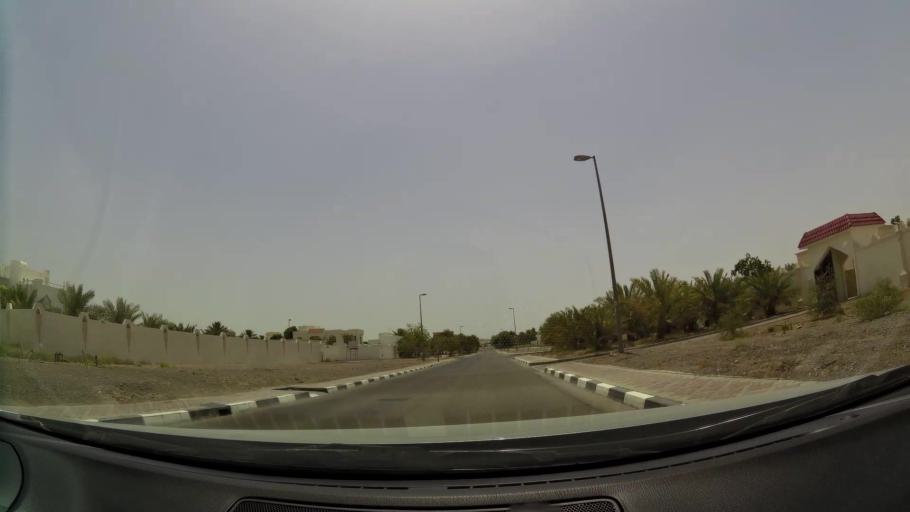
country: AE
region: Abu Dhabi
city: Al Ain
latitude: 24.1996
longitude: 55.7332
